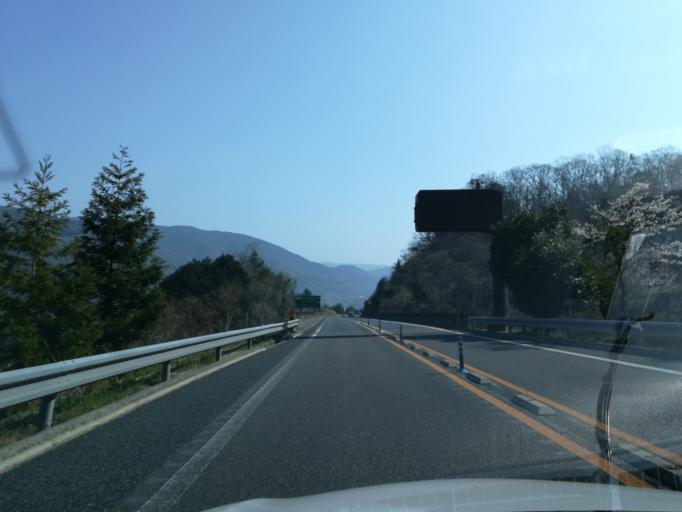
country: JP
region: Tokushima
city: Ikedacho
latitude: 34.0226
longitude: 133.8166
